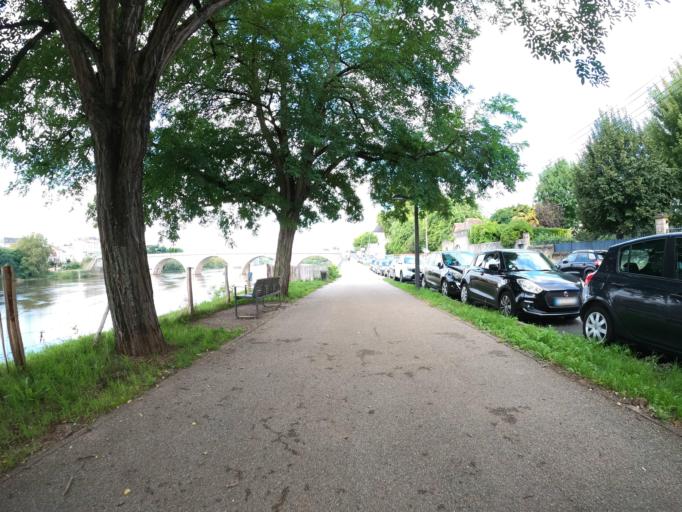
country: FR
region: Aquitaine
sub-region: Departement de la Dordogne
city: Bergerac
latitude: 44.8475
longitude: 0.4858
